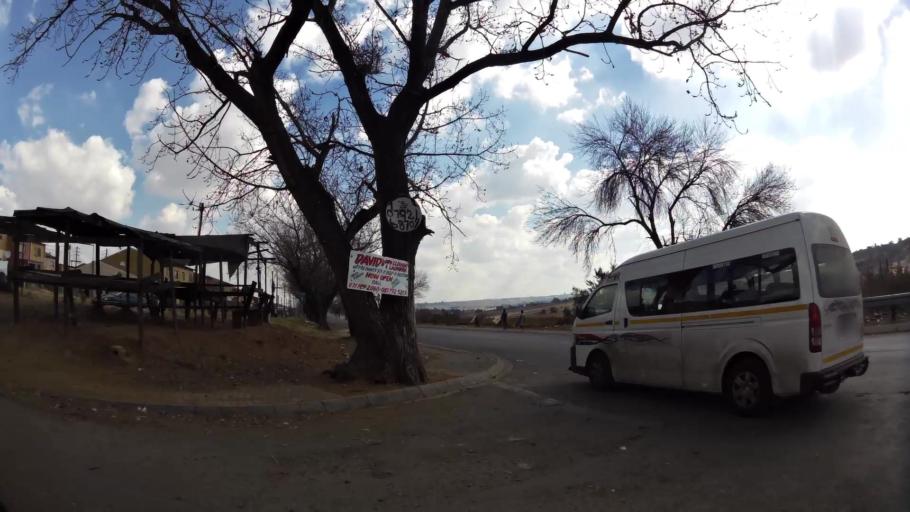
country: ZA
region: Gauteng
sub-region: City of Johannesburg Metropolitan Municipality
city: Roodepoort
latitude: -26.1818
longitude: 27.8516
